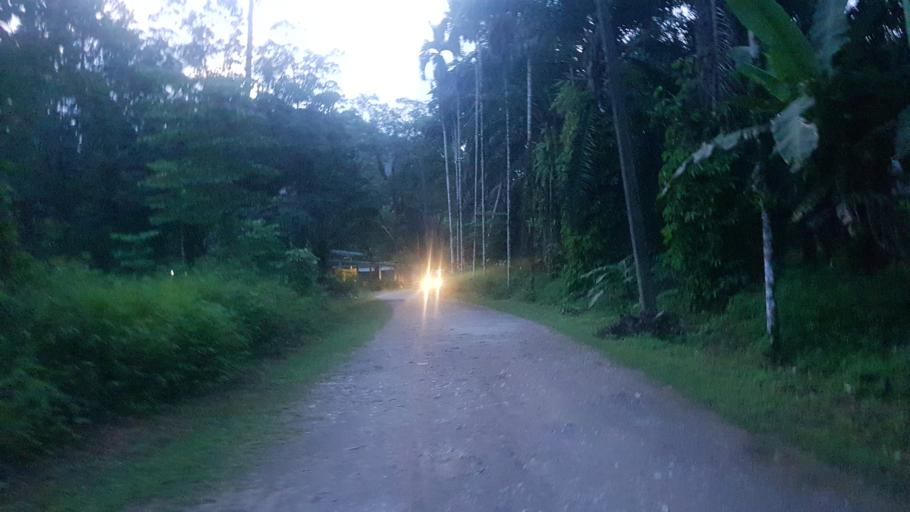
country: TH
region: Phangnga
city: Takua Pa
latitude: 8.9086
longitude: 98.5284
